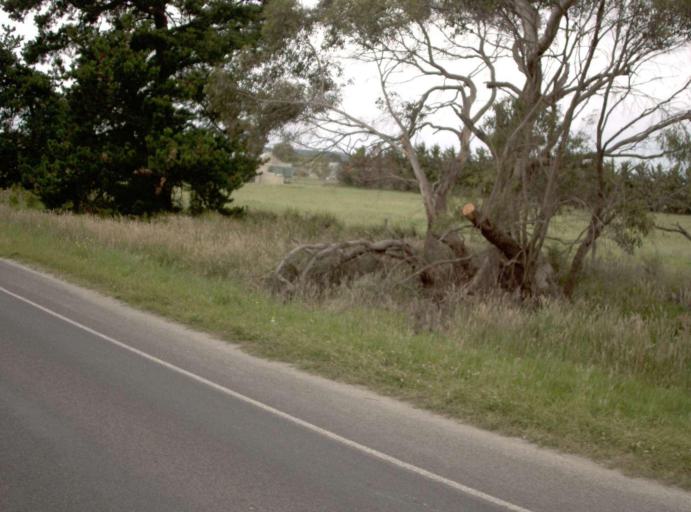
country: AU
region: Victoria
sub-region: Cardinia
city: Koo-Wee-Rup
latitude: -38.3251
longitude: 145.5881
